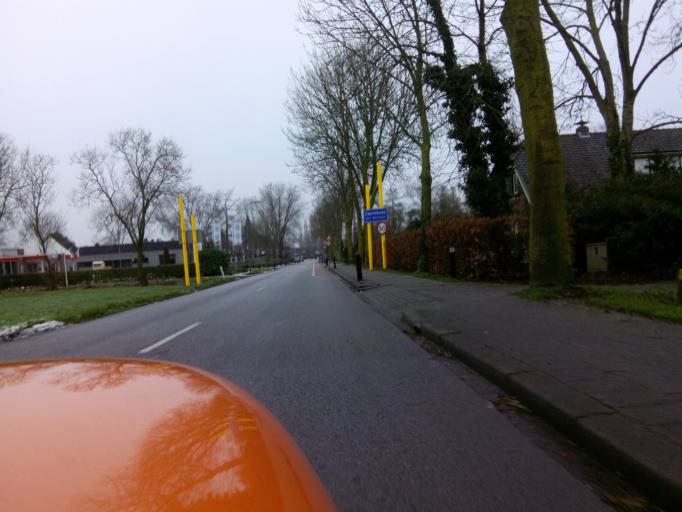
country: NL
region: Gelderland
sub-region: Gemeente Barneveld
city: Zwartebroek
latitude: 52.1768
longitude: 5.5091
